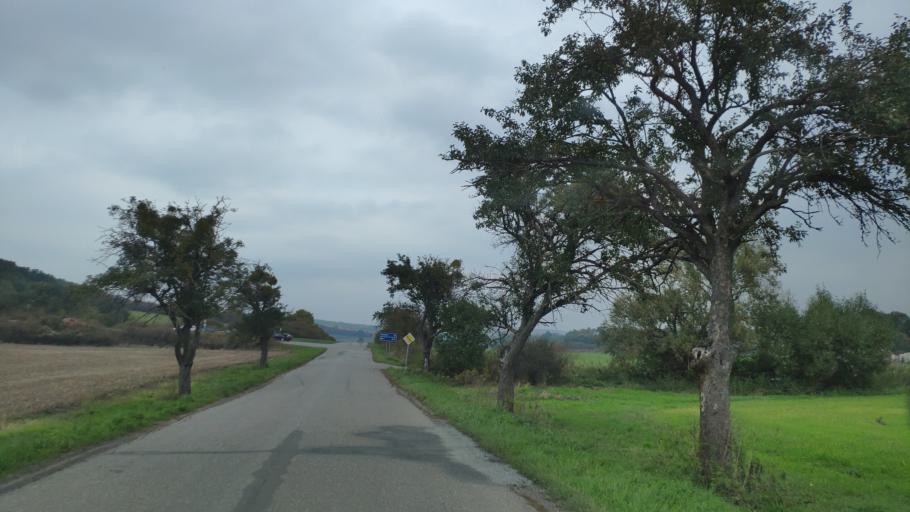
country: SK
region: Kosicky
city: Kosice
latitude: 48.6421
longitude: 21.3737
